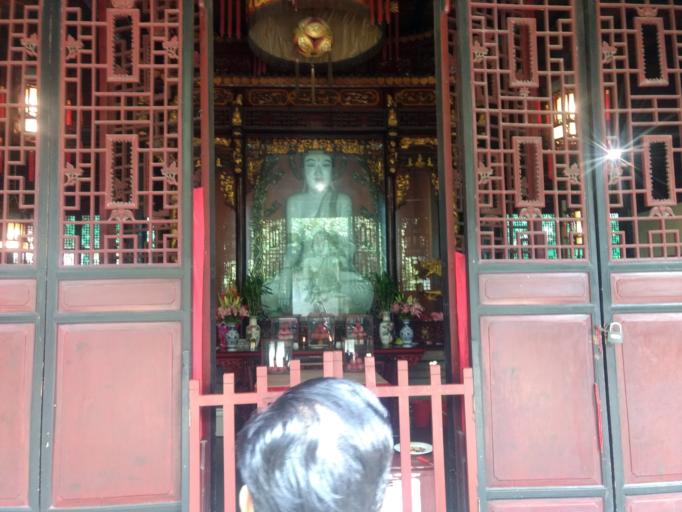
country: CN
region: Sichuan
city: Chengdu
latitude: 30.6774
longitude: 104.0704
